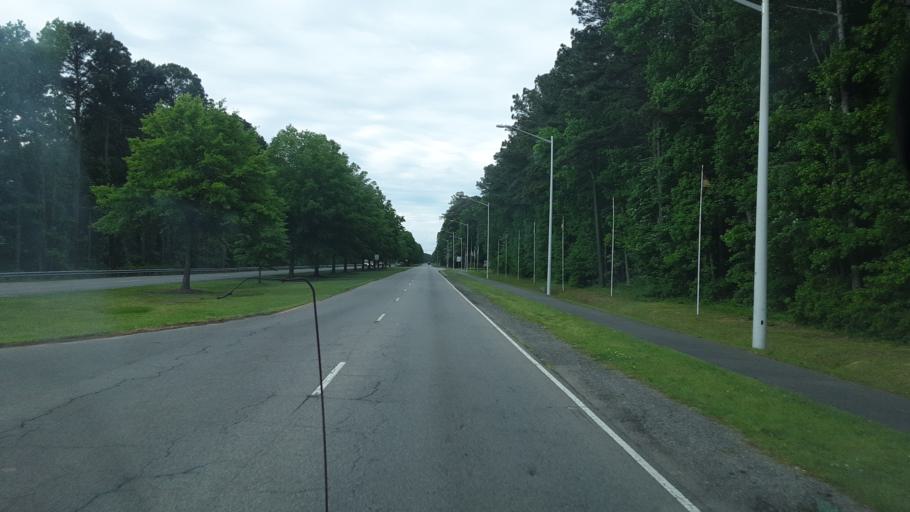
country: US
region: Virginia
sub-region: City of Virginia Beach
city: Virginia Beach
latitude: 36.8079
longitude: -75.9909
